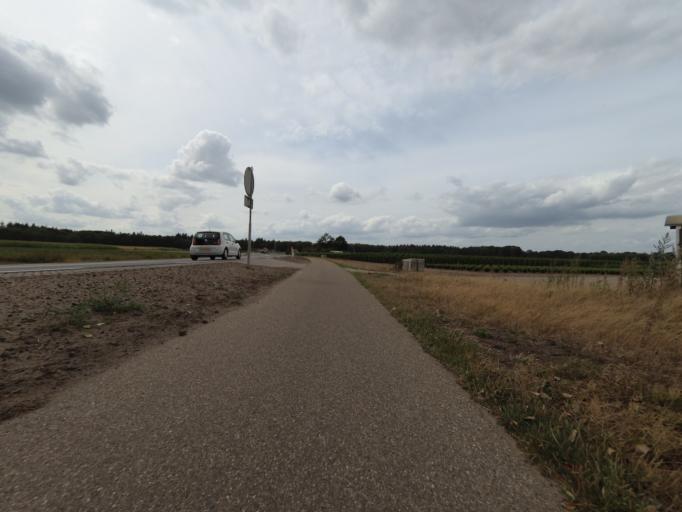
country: NL
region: Overijssel
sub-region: Gemeente Enschede
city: Enschede
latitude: 52.2646
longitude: 6.8715
